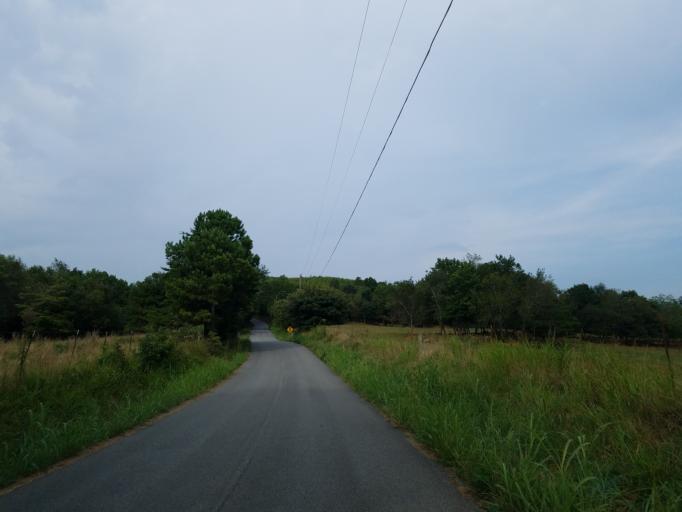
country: US
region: Georgia
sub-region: Bartow County
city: Rydal
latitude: 34.3688
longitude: -84.6905
